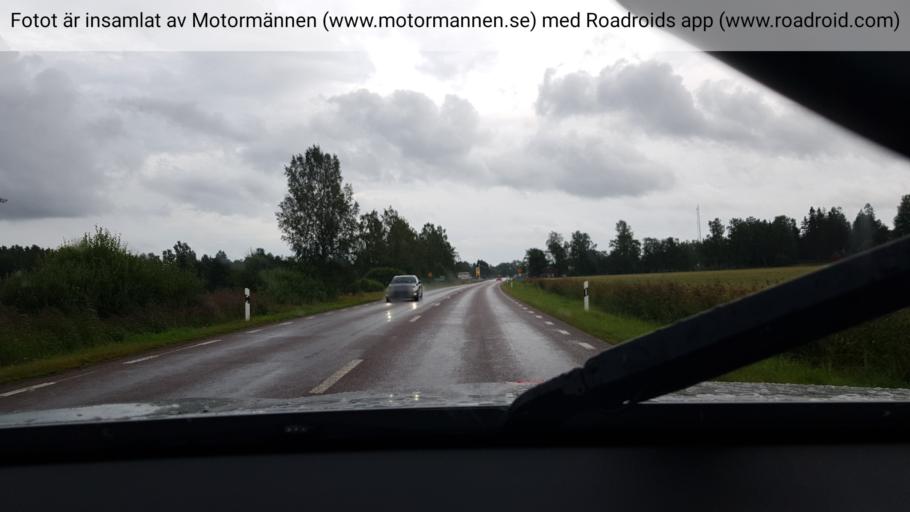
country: SE
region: Uppsala
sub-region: Tierps Kommun
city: Karlholmsbruk
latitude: 60.4788
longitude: 17.7545
